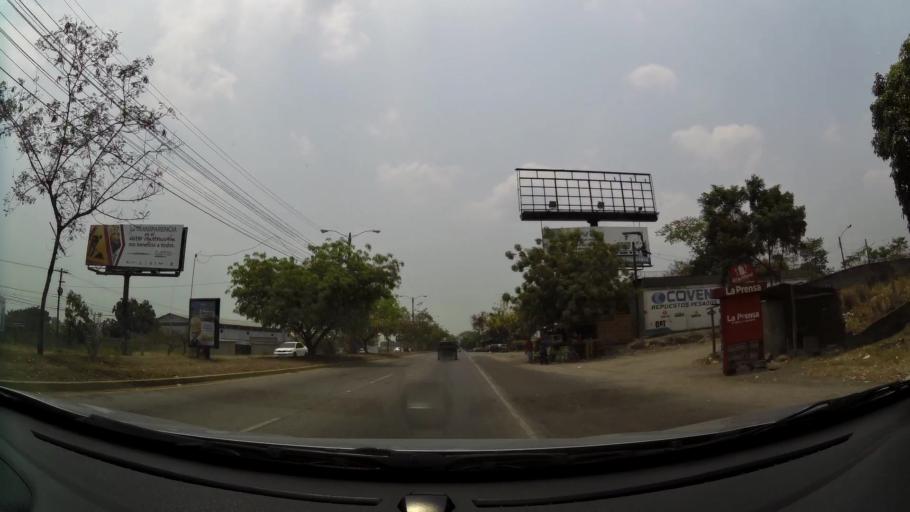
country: HN
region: Cortes
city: Chotepe
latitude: 15.4623
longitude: -87.9594
